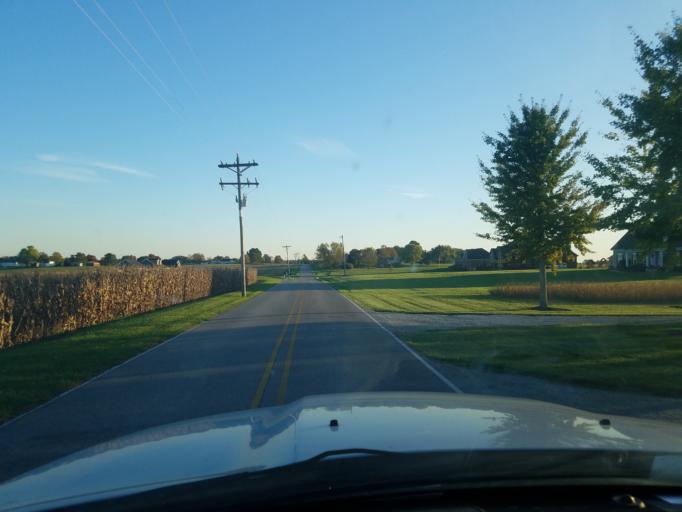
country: US
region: Indiana
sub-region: Floyd County
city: Galena
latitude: 38.4097
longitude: -85.9109
